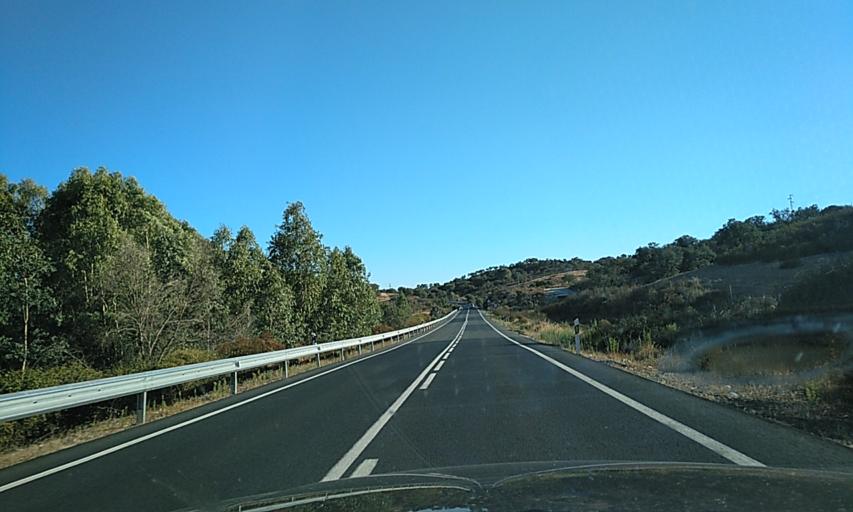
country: ES
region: Andalusia
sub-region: Provincia de Huelva
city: Alosno
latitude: 37.5265
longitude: -7.1345
